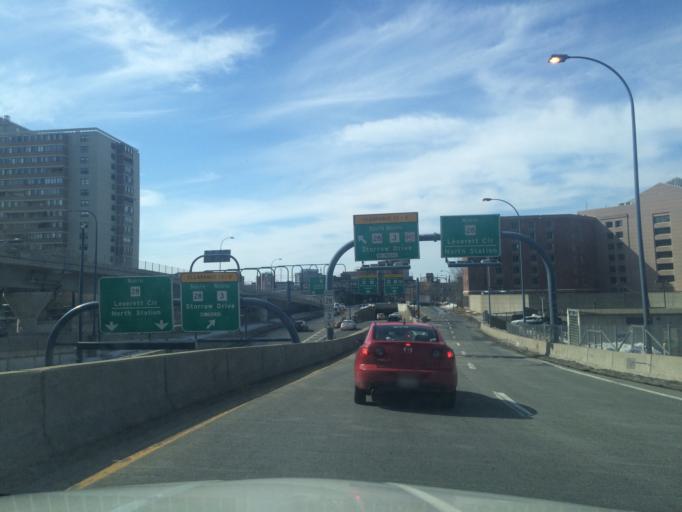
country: US
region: Massachusetts
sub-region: Suffolk County
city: Boston
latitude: 42.3663
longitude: -71.0646
